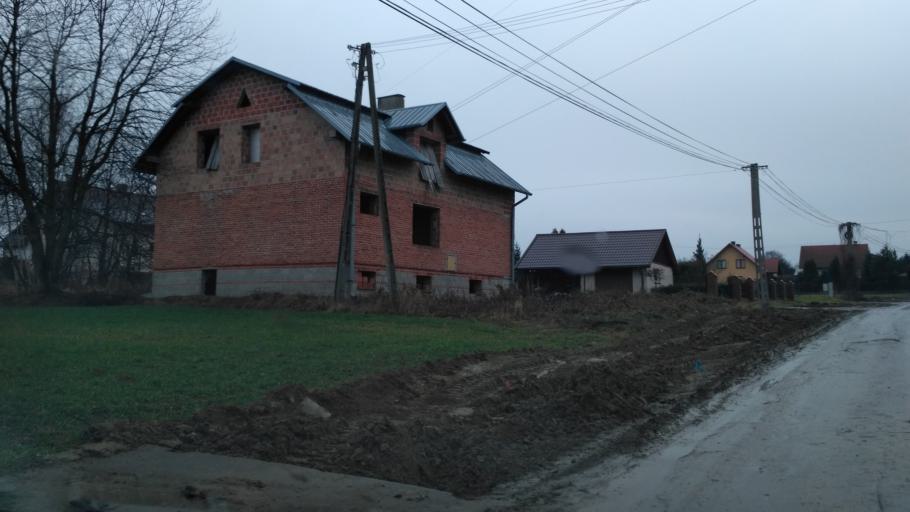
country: PL
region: Subcarpathian Voivodeship
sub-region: Powiat rzeszowski
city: Tyczyn
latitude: 49.9689
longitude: 21.9955
